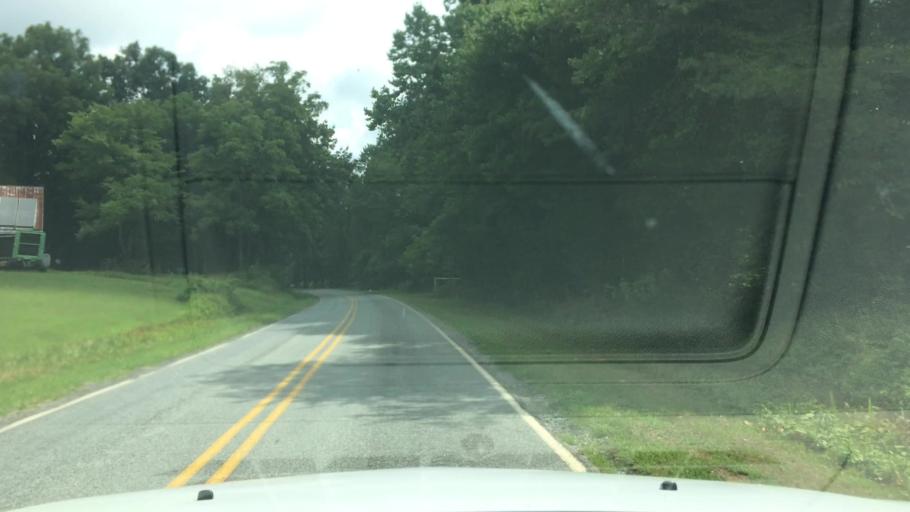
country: US
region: North Carolina
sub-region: Yadkin County
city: Jonesville
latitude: 36.1053
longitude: -80.8583
